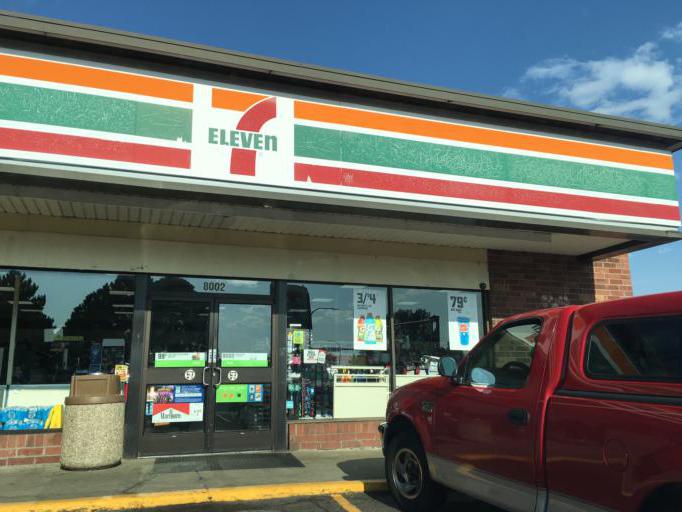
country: US
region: Colorado
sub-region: Adams County
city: Westminster
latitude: 39.8422
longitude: -105.0572
